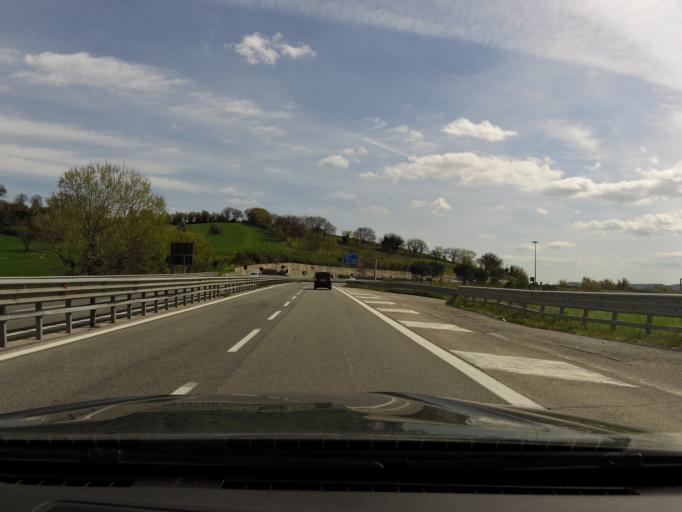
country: IT
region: The Marches
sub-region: Provincia di Ancona
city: San Biagio
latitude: 43.5378
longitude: 13.5170
